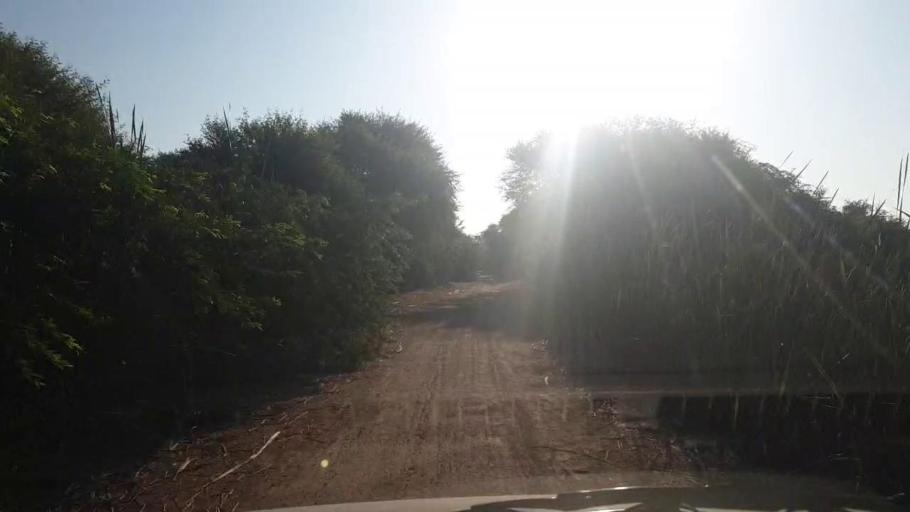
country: PK
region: Sindh
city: Talhar
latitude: 24.8077
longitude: 68.8479
